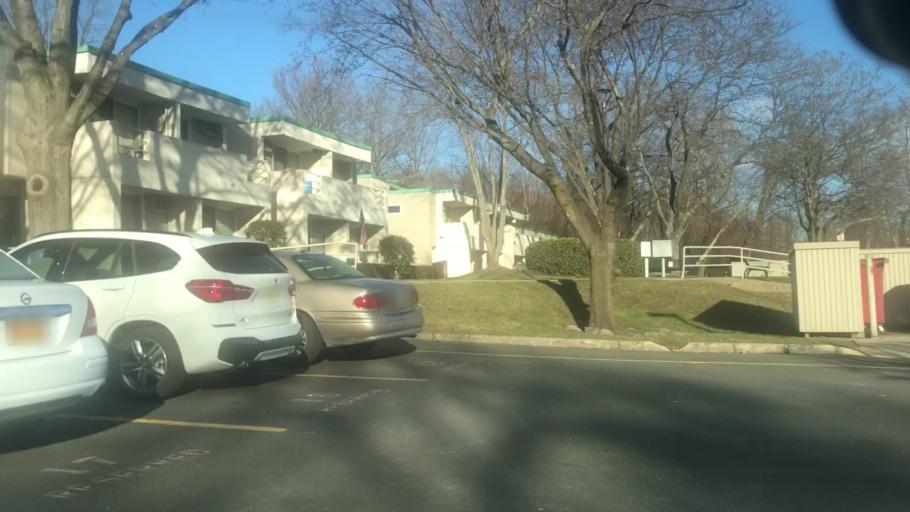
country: US
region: New York
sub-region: Rockland County
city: West Haverstraw
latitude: 41.2142
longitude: -73.9852
